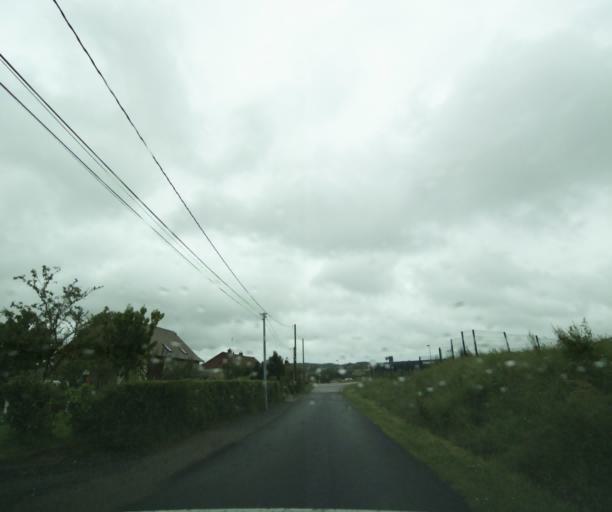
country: FR
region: Bourgogne
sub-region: Departement de Saone-et-Loire
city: Charolles
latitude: 46.4808
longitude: 4.4316
